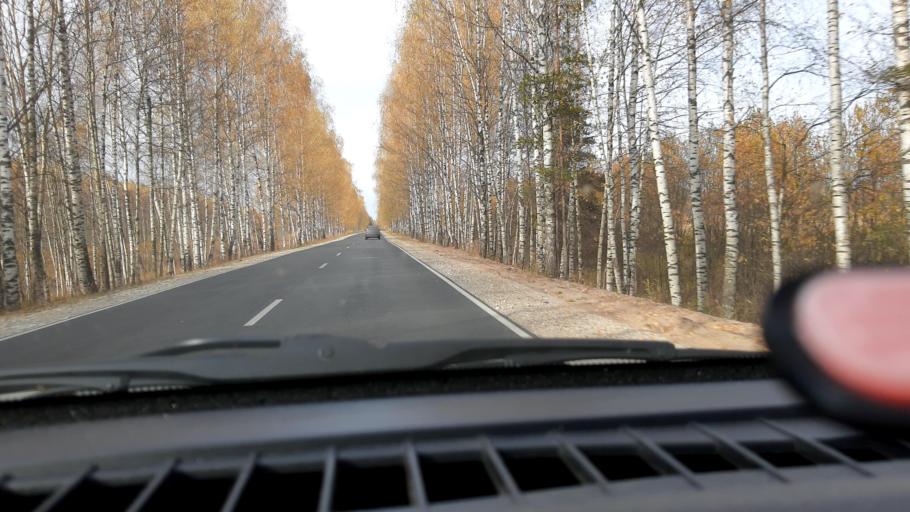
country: RU
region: Nizjnij Novgorod
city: Neklyudovo
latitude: 56.4904
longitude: 43.8611
